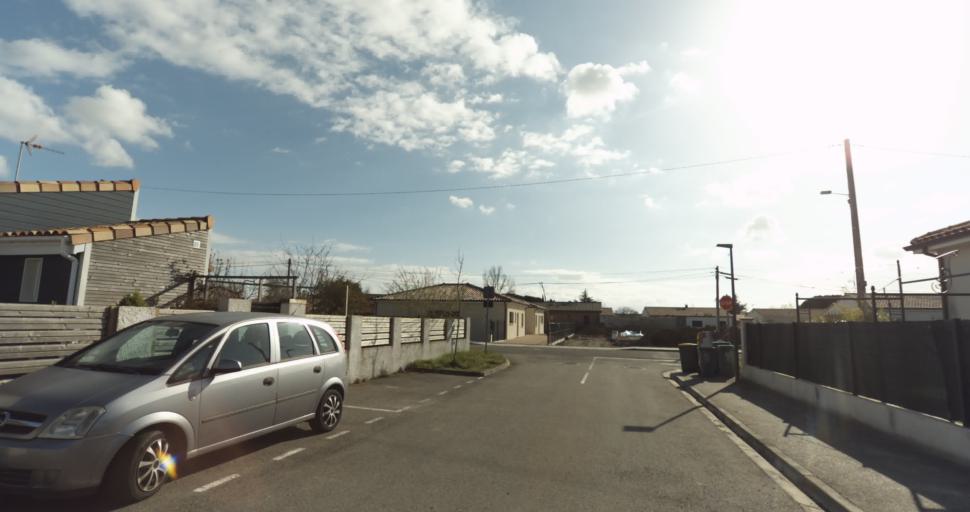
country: FR
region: Midi-Pyrenees
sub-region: Departement de la Haute-Garonne
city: Auterive
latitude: 43.3438
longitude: 1.4871
